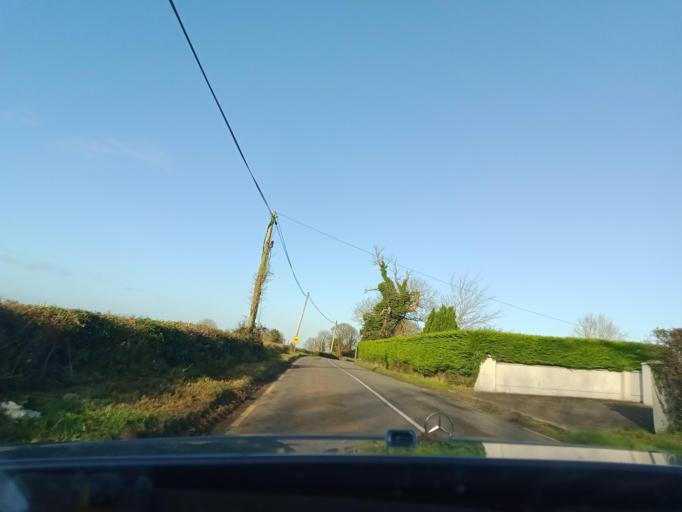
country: IE
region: Leinster
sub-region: Kilkenny
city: Callan
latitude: 52.5100
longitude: -7.3845
